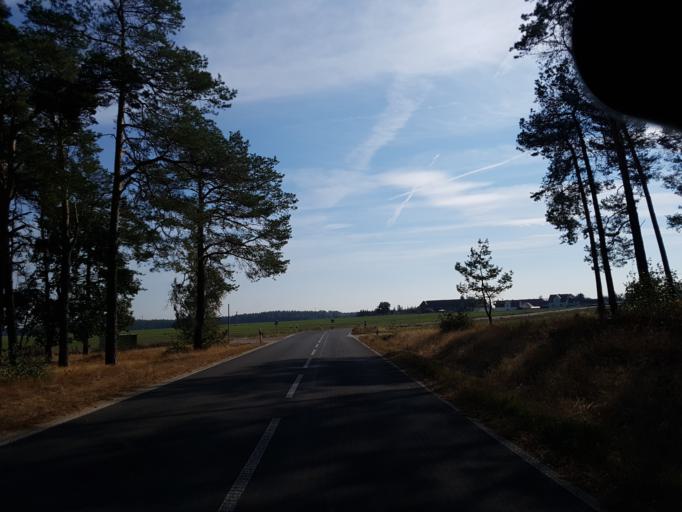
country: DE
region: Brandenburg
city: Schonborn
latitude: 51.6744
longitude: 13.4719
